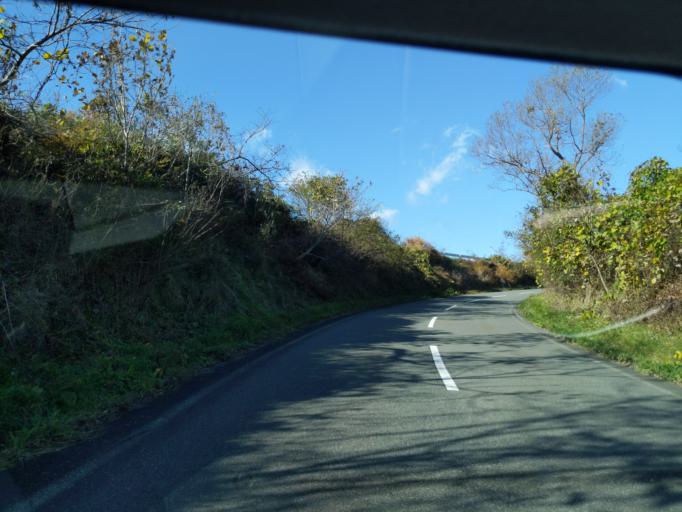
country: JP
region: Iwate
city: Mizusawa
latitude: 39.0934
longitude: 141.1227
